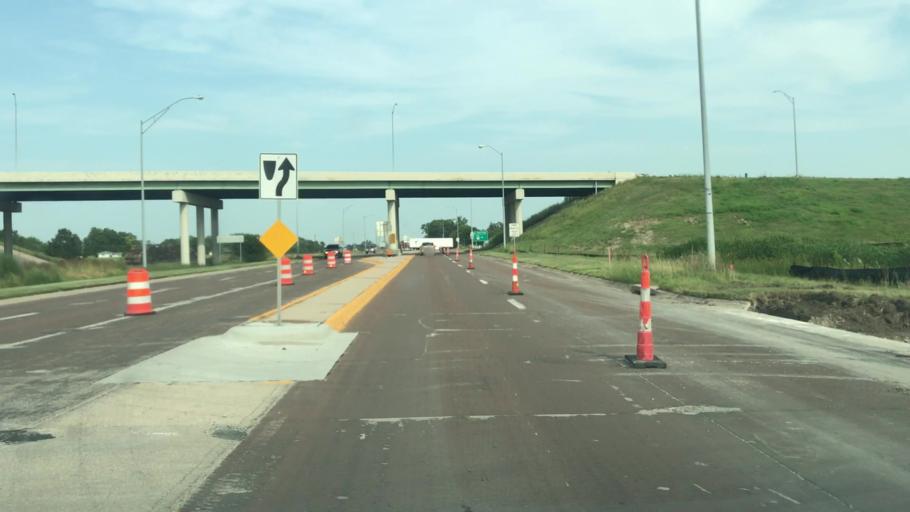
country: US
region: Nebraska
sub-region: Hall County
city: Grand Island
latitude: 40.9538
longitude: -98.3856
